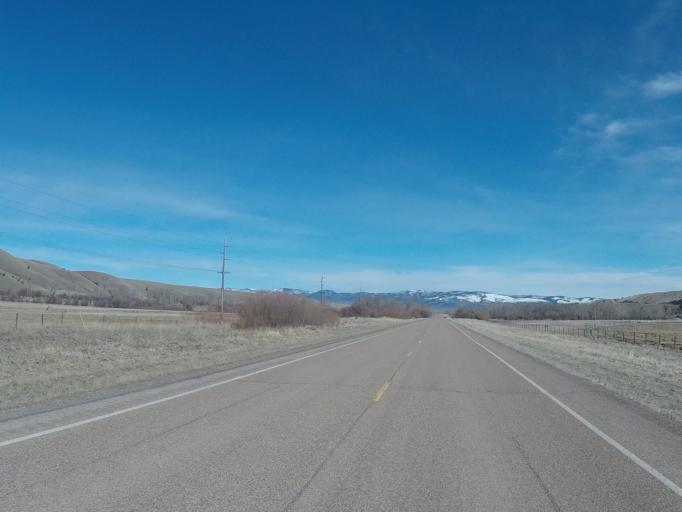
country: US
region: Montana
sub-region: Granite County
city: Philipsburg
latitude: 46.5246
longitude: -113.2250
